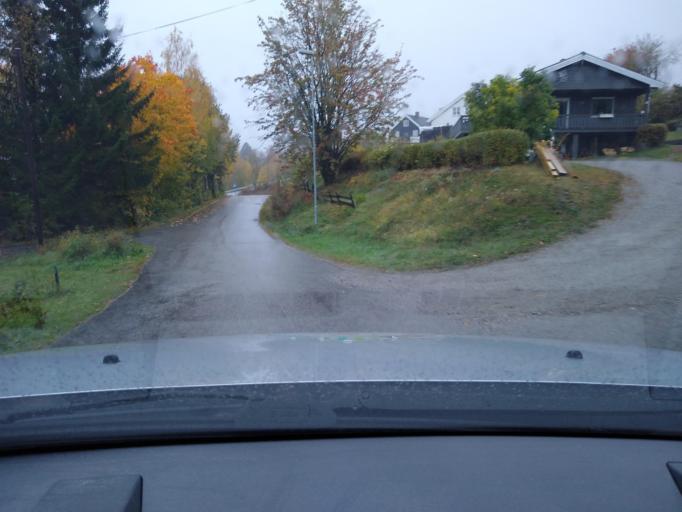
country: NO
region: Oppland
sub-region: Ringebu
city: Ringebu
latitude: 61.5327
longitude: 10.1468
